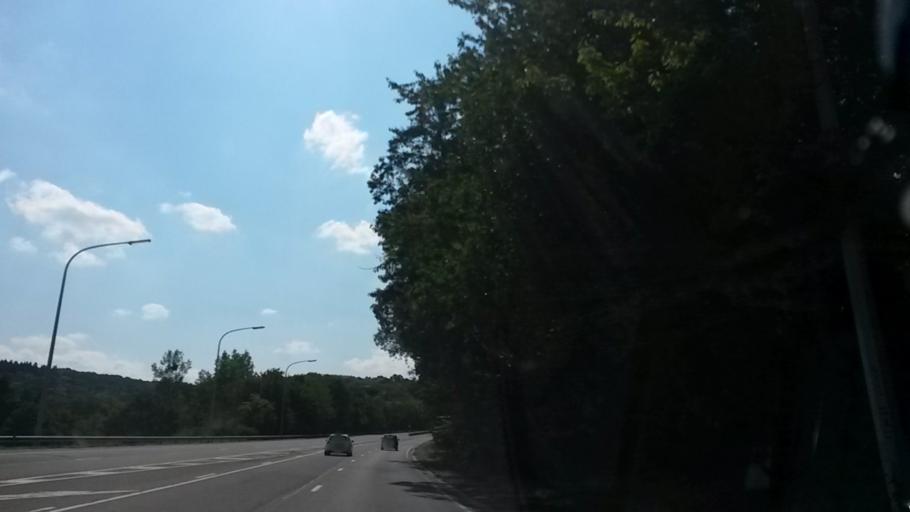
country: BE
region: Wallonia
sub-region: Province de Namur
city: Fosses-la-Ville
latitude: 50.4452
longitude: 4.7040
